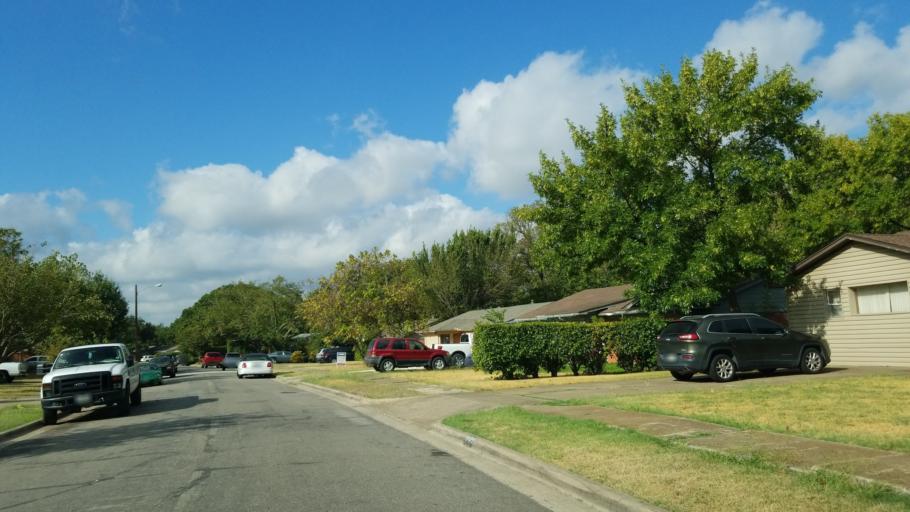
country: US
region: Texas
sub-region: Dallas County
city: Richardson
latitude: 32.9310
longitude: -96.7704
